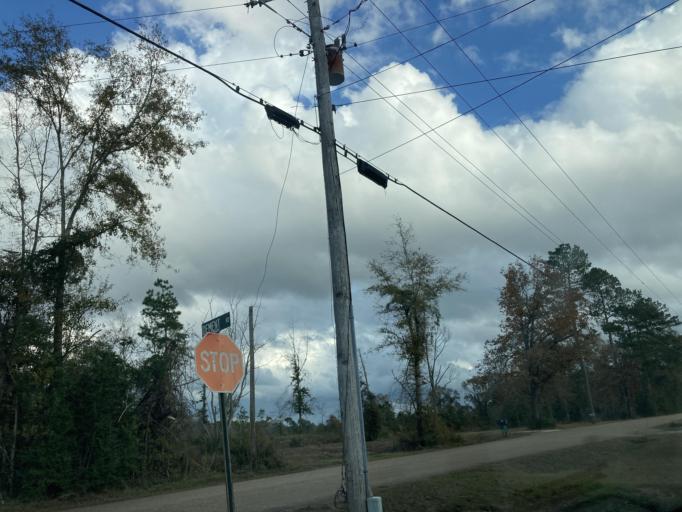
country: US
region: Mississippi
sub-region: Lamar County
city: Purvis
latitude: 31.1340
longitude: -89.6179
